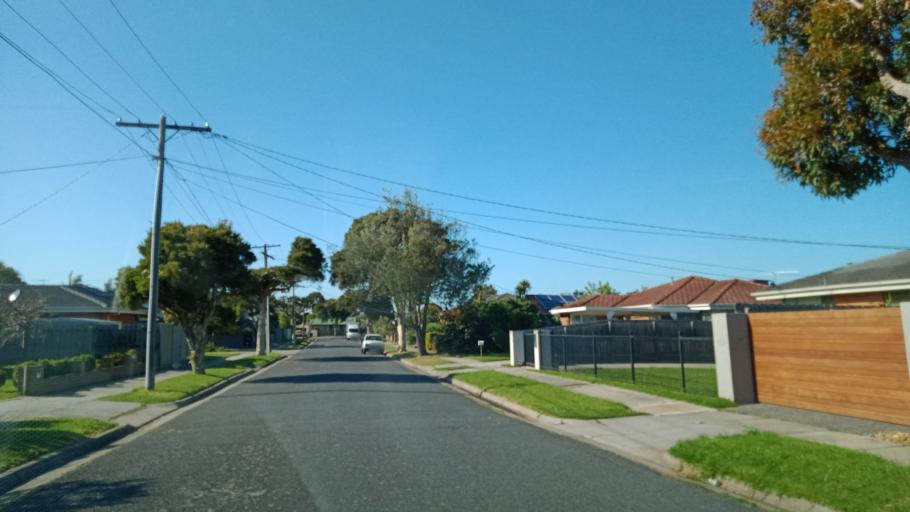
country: AU
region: Victoria
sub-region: Kingston
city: Chelsea Heights
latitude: -38.0417
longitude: 145.1307
